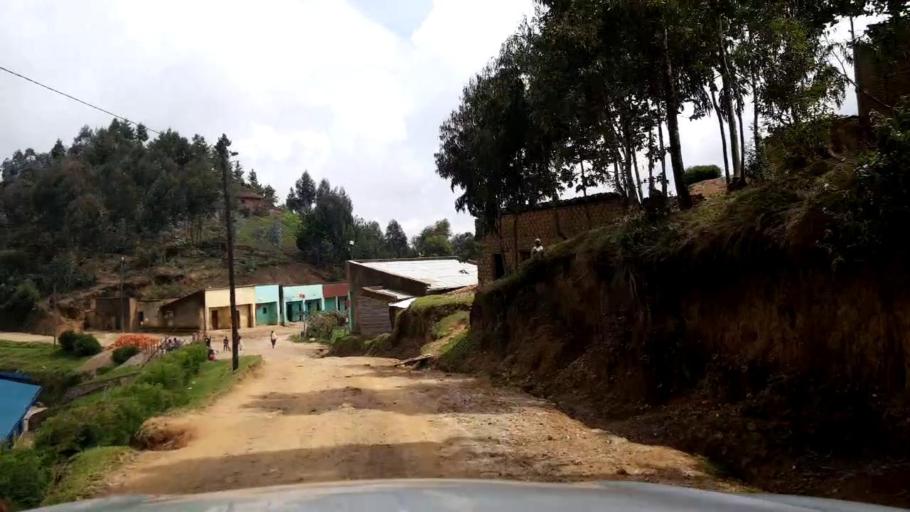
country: RW
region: Western Province
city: Kibuye
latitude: -1.9369
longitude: 29.4567
